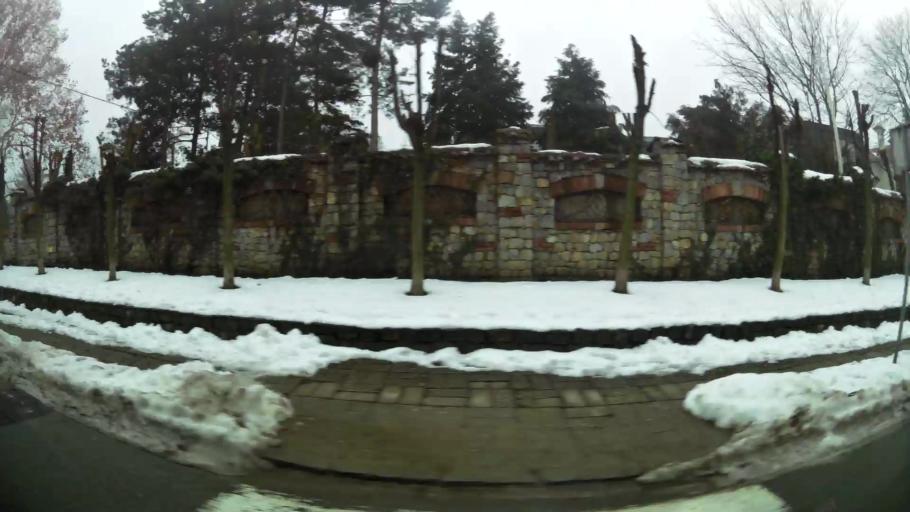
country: RS
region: Central Serbia
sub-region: Belgrade
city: Cukarica
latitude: 44.7917
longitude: 20.4351
